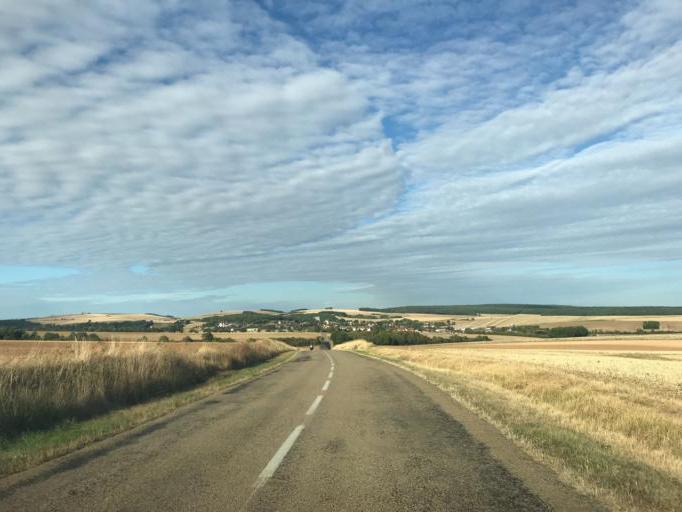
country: FR
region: Bourgogne
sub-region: Departement de l'Yonne
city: Fontenailles
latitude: 47.6036
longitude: 3.4842
